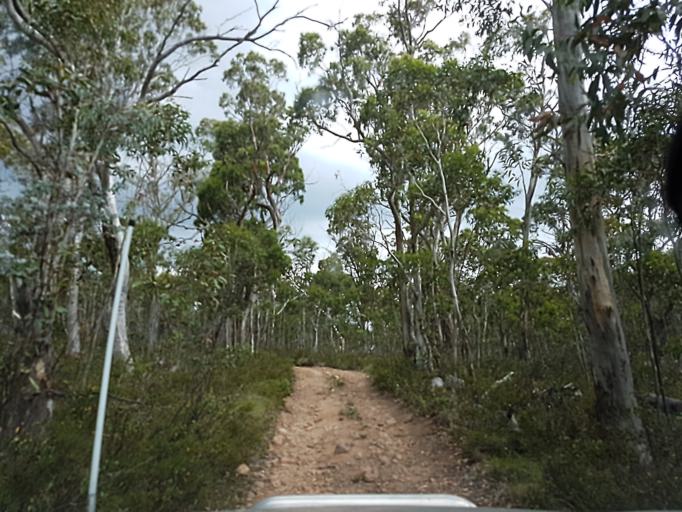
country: AU
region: New South Wales
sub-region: Snowy River
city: Jindabyne
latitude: -36.8792
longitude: 148.1806
